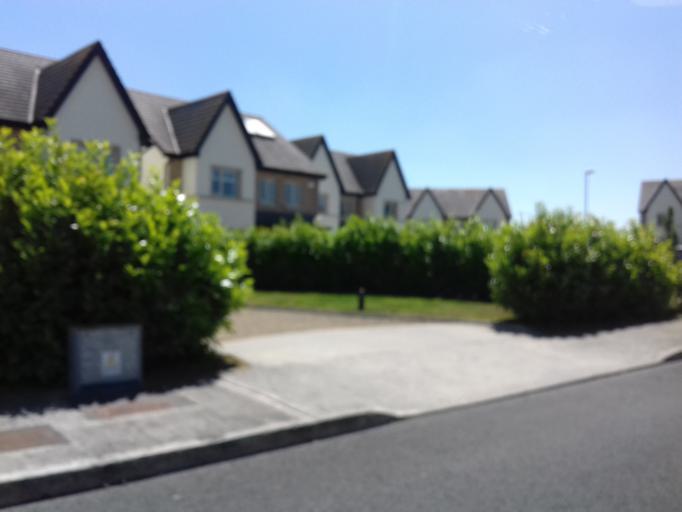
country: IE
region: Leinster
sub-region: Fingal County
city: Swords
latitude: 53.5175
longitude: -6.2689
